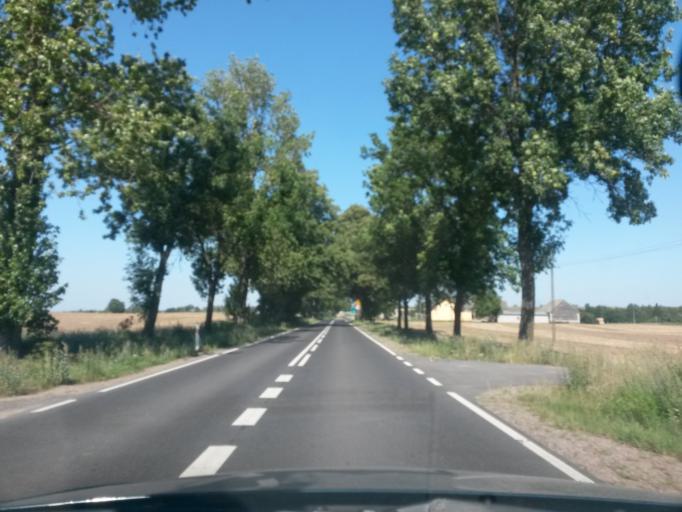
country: PL
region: Warmian-Masurian Voivodeship
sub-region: Powiat ilawski
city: Lubawa
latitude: 53.4050
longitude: 19.7985
